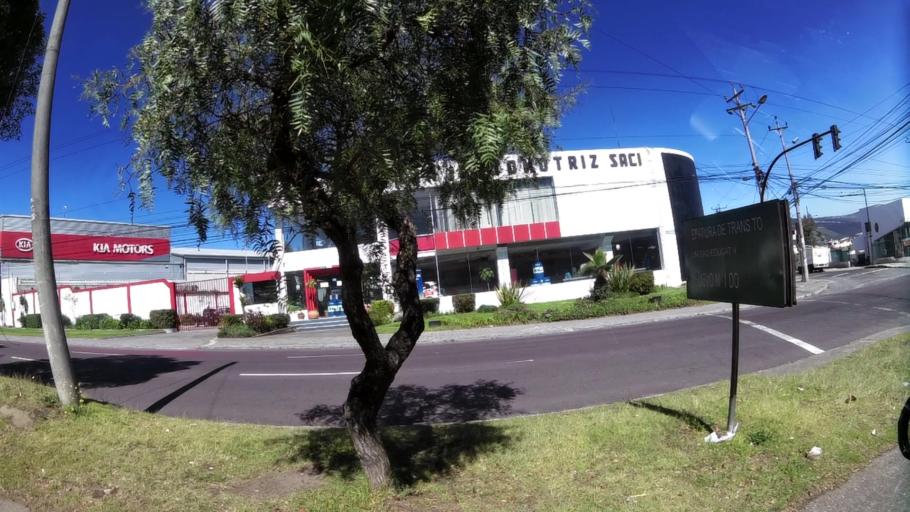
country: EC
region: Pichincha
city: Quito
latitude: -0.1266
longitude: -78.4779
